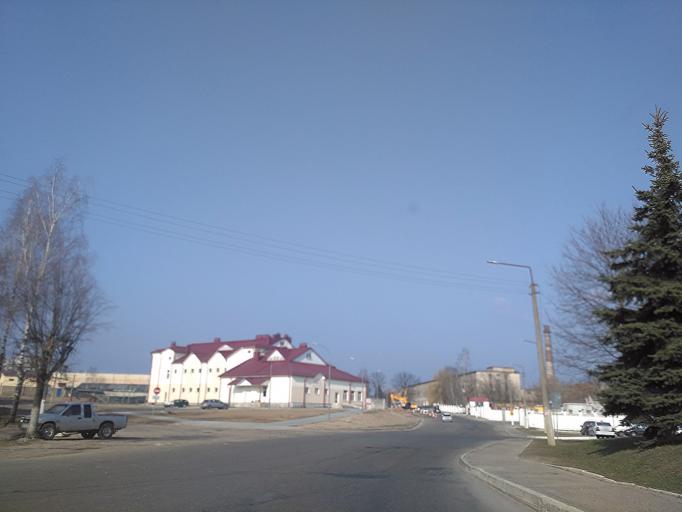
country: BY
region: Minsk
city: Horad Barysaw
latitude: 54.2271
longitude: 28.5220
